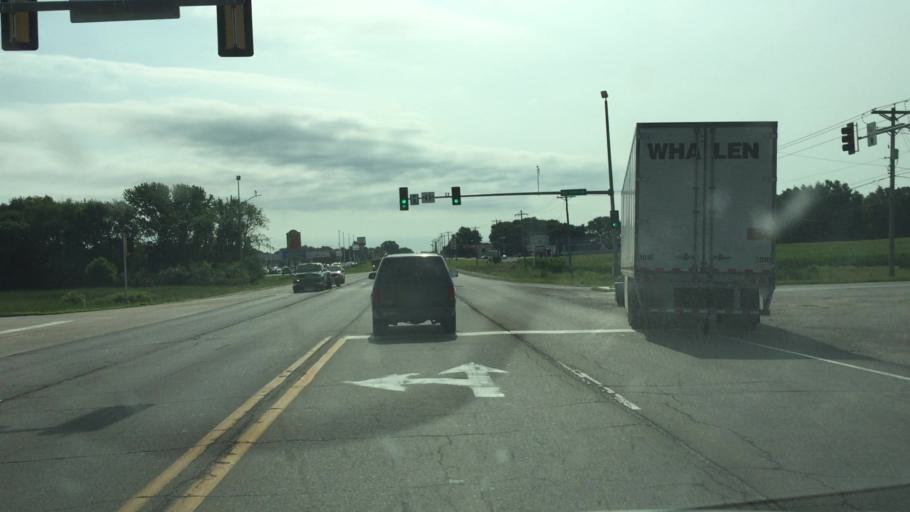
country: US
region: Iowa
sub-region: Lee County
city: Fort Madison
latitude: 40.6241
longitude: -91.3825
